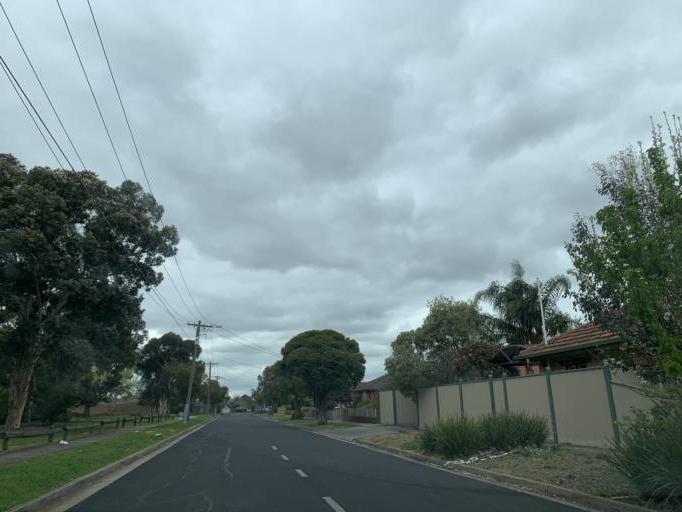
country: AU
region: Victoria
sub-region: Moreland
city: Pascoe Vale
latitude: -37.7310
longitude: 144.9424
